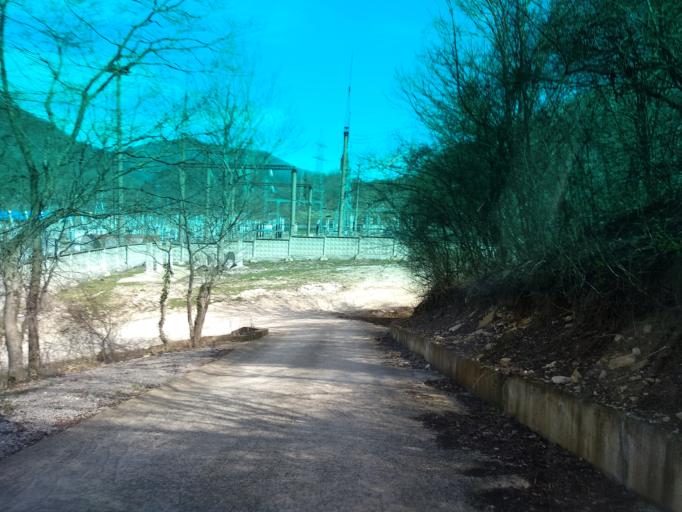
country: RU
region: Krasnodarskiy
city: Shepsi
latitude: 44.0525
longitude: 39.1639
